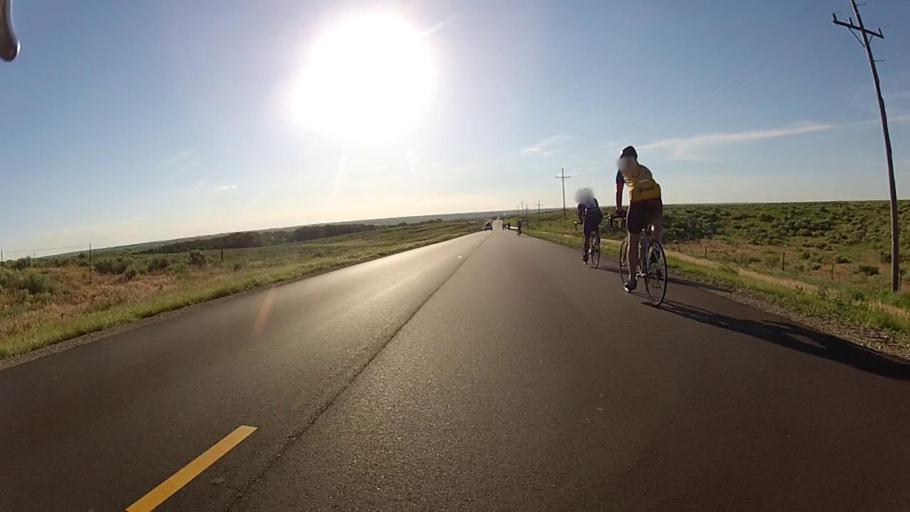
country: US
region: Kansas
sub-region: Comanche County
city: Coldwater
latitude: 37.2821
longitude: -99.0967
